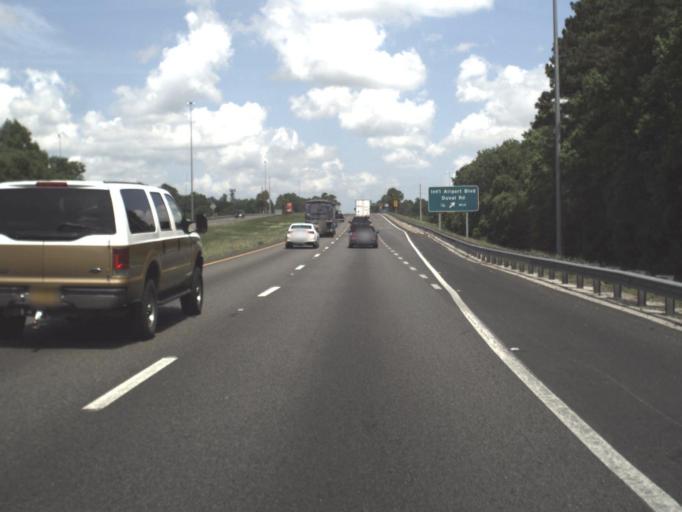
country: US
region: Florida
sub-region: Duval County
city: Jacksonville
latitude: 30.4600
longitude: -81.6833
